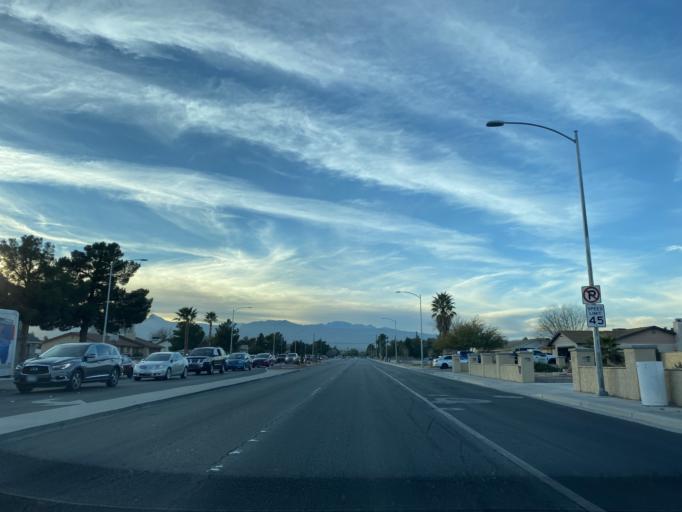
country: US
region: Nevada
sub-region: Clark County
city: Las Vegas
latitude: 36.2622
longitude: -115.2344
